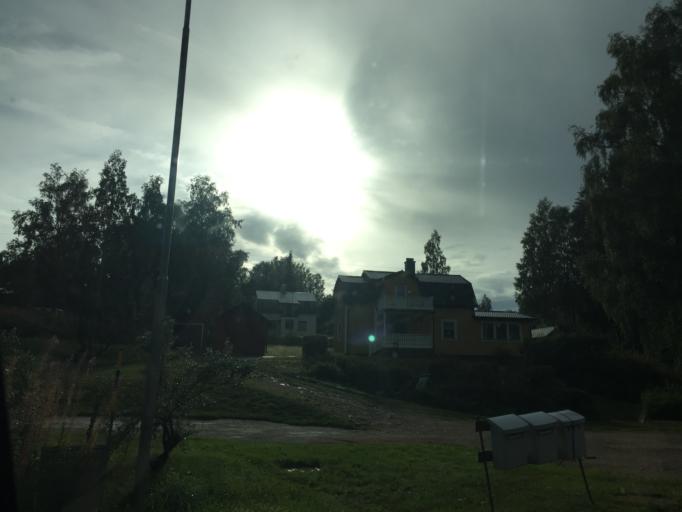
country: SE
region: Vaermland
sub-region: Filipstads Kommun
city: Lesjofors
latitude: 59.9759
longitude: 14.1832
